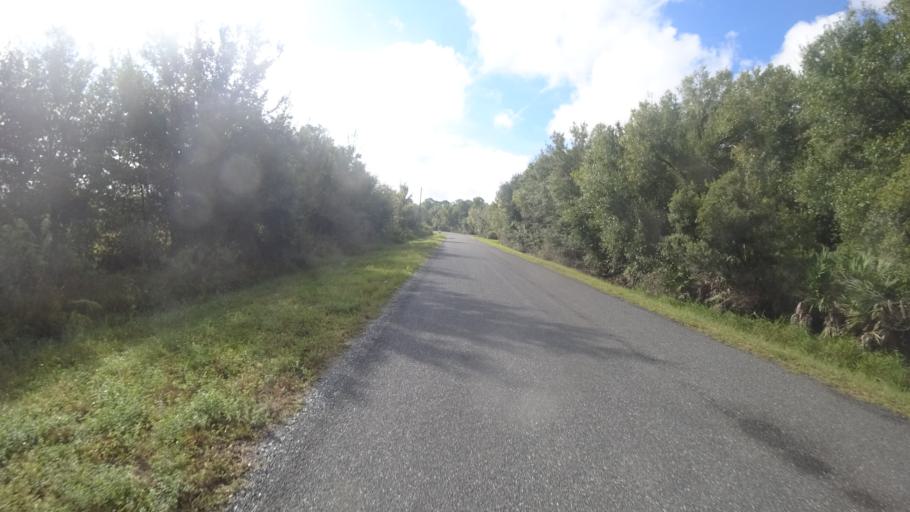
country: US
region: Florida
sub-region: Hillsborough County
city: Wimauma
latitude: 27.4757
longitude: -82.1539
